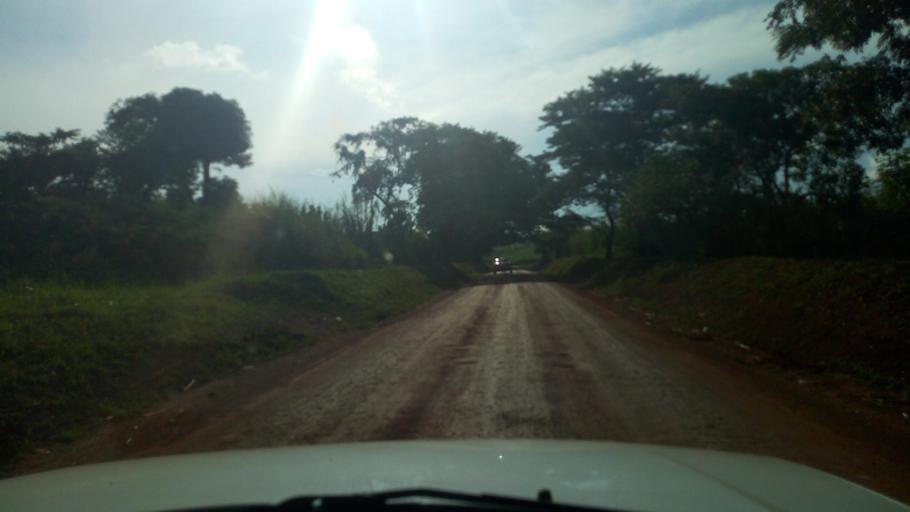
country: UG
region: Western Region
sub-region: Masindi District
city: Masindi
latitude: 1.6740
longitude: 31.6587
